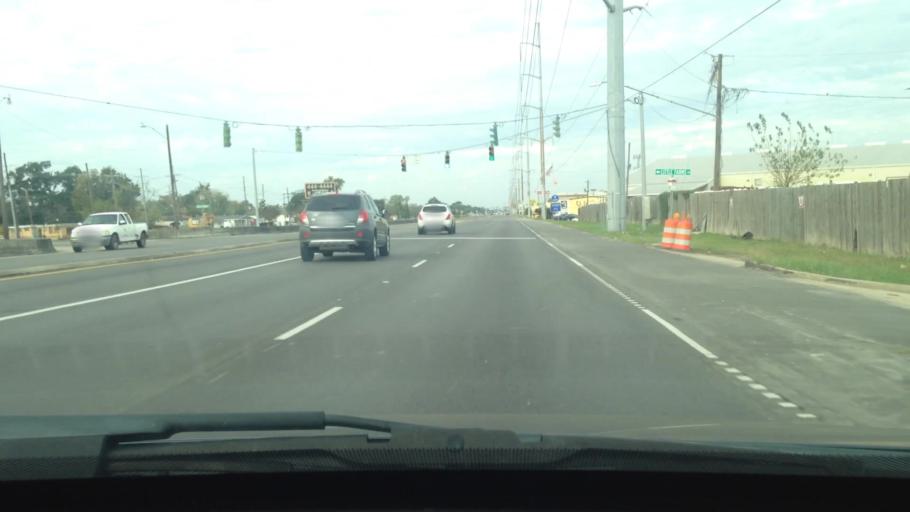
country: US
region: Louisiana
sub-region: Jefferson Parish
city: River Ridge
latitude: 29.9780
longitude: -90.2125
